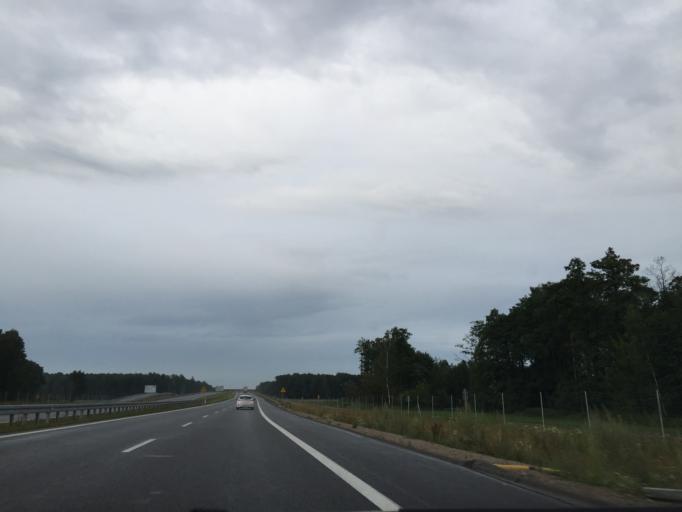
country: PL
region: Podlasie
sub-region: Powiat zambrowski
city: Zambrow
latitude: 53.0200
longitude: 22.3158
